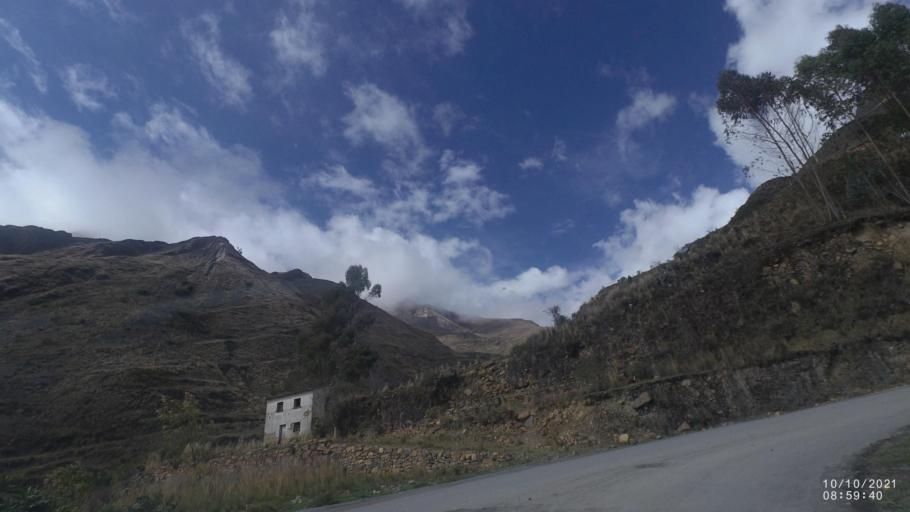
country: BO
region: La Paz
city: Quime
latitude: -16.9976
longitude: -67.2603
